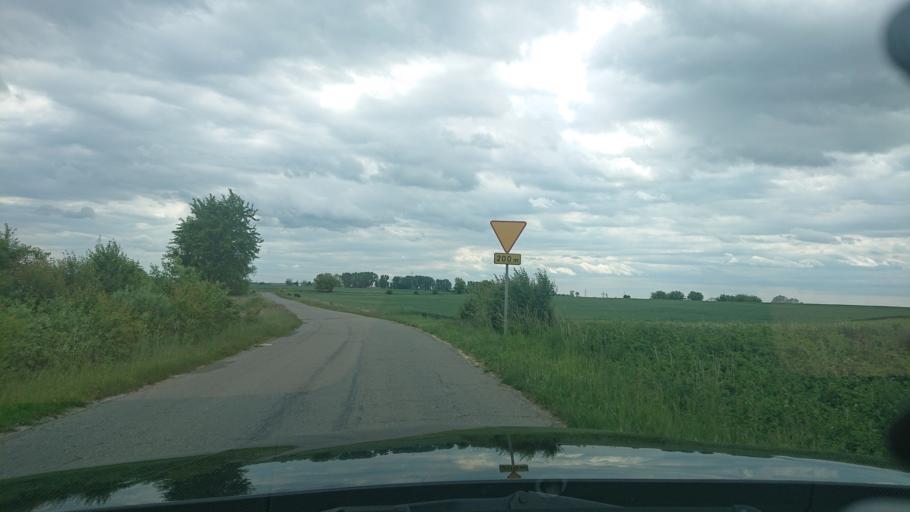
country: PL
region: Greater Poland Voivodeship
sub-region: Powiat gnieznienski
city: Gniezno
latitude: 52.5388
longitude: 17.5347
